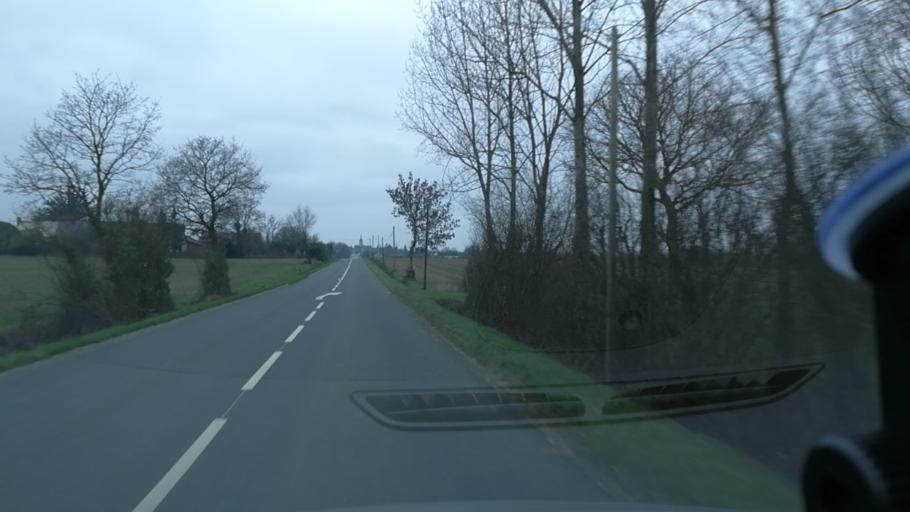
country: FR
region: Brittany
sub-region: Departement d'Ille-et-Vilaine
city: Tresboeuf
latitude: 47.8821
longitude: -1.5322
